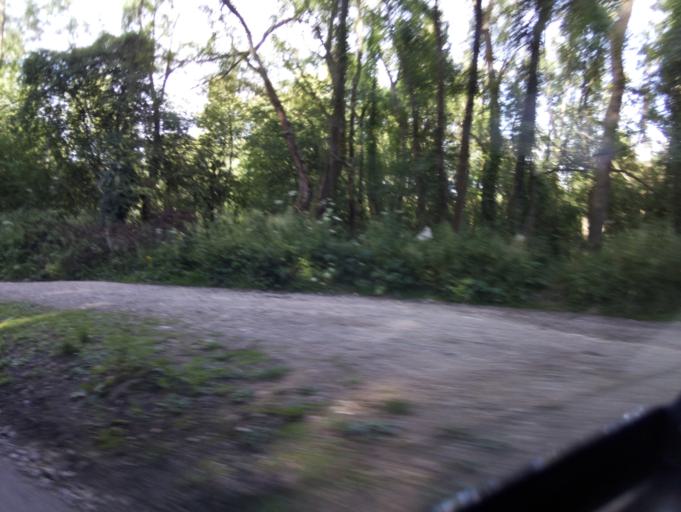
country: GB
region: England
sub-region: Gloucestershire
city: Painswick
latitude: 51.7808
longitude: -2.2432
